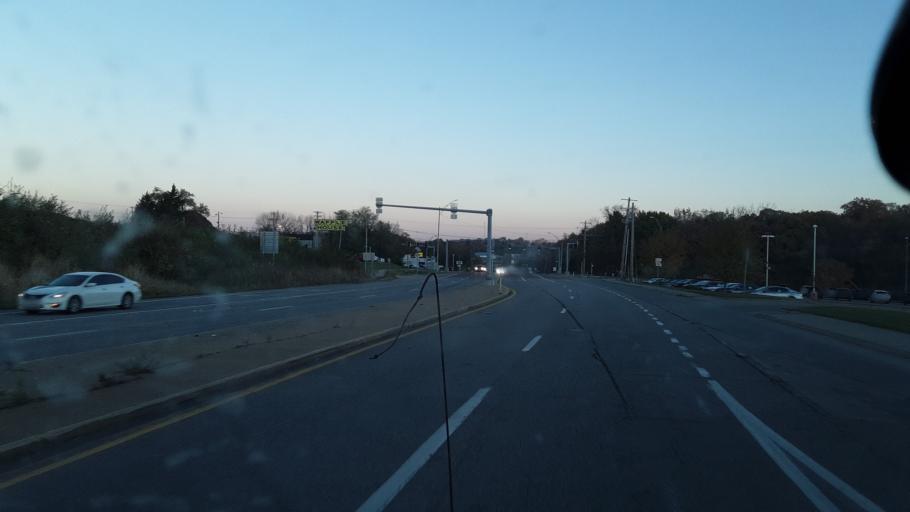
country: US
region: Missouri
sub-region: Boone County
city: Columbia
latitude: 38.9696
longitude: -92.3251
